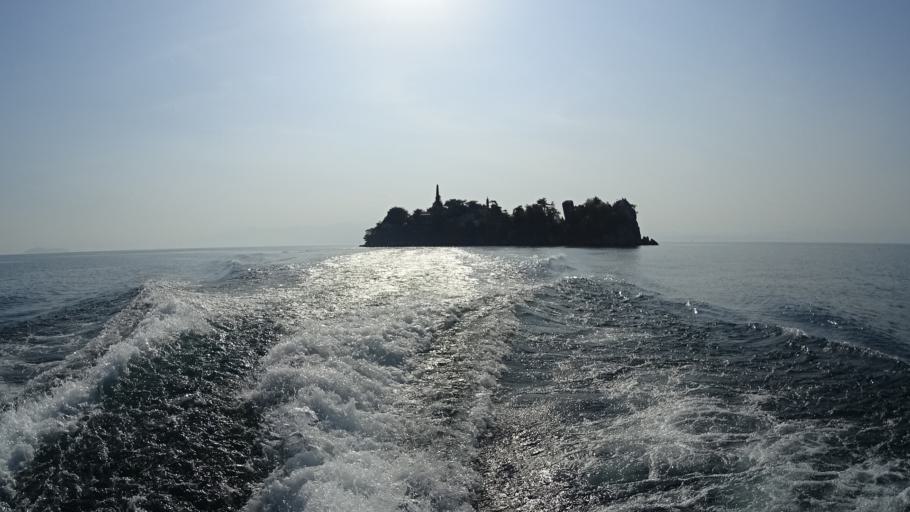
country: JP
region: Shiga Prefecture
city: Hikone
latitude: 35.2964
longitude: 136.1814
